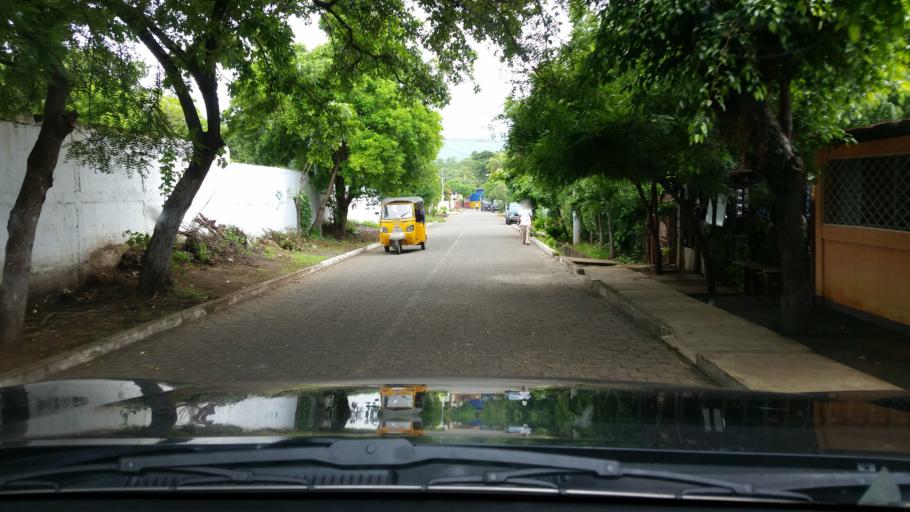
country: NI
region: Masaya
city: Ticuantepe
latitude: 12.0229
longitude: -86.2070
